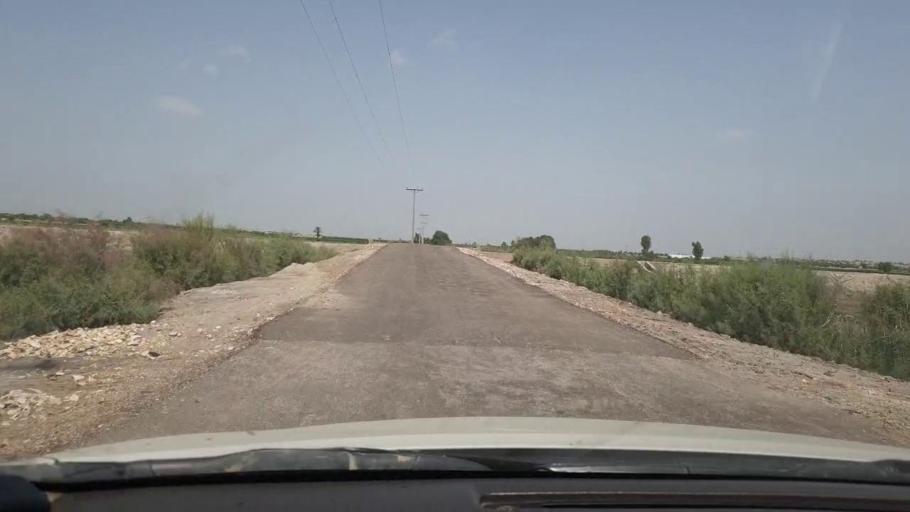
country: PK
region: Sindh
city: Rohri
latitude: 27.4824
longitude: 69.0558
